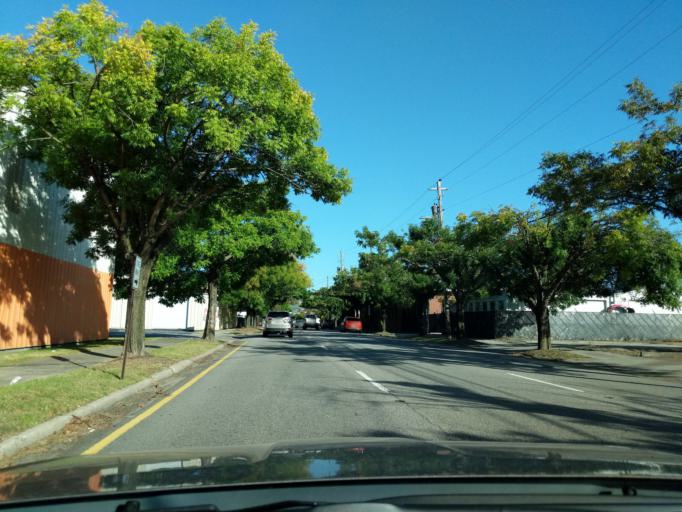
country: US
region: Georgia
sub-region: Richmond County
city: Augusta
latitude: 33.4803
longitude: -81.9777
